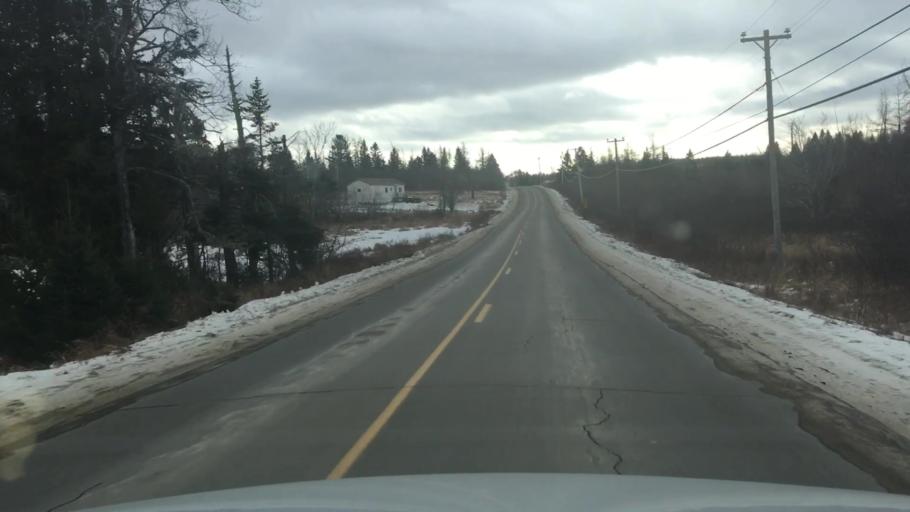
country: US
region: Maine
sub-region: Washington County
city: Machias
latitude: 44.6831
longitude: -67.4671
